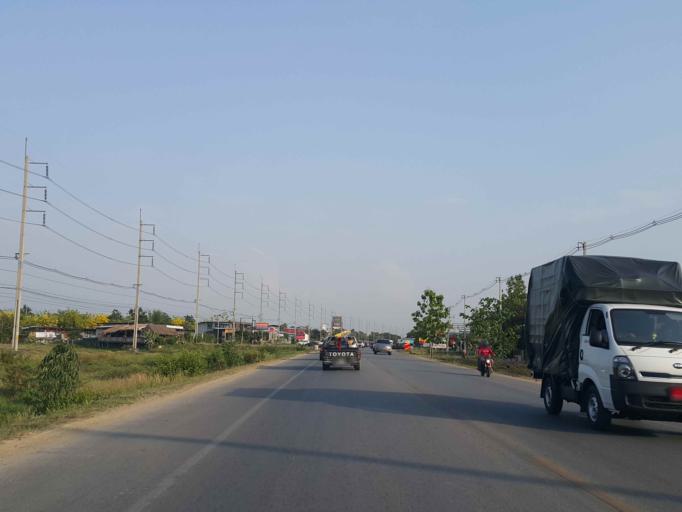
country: TH
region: Chiang Mai
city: San Sai
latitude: 18.7929
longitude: 99.0678
